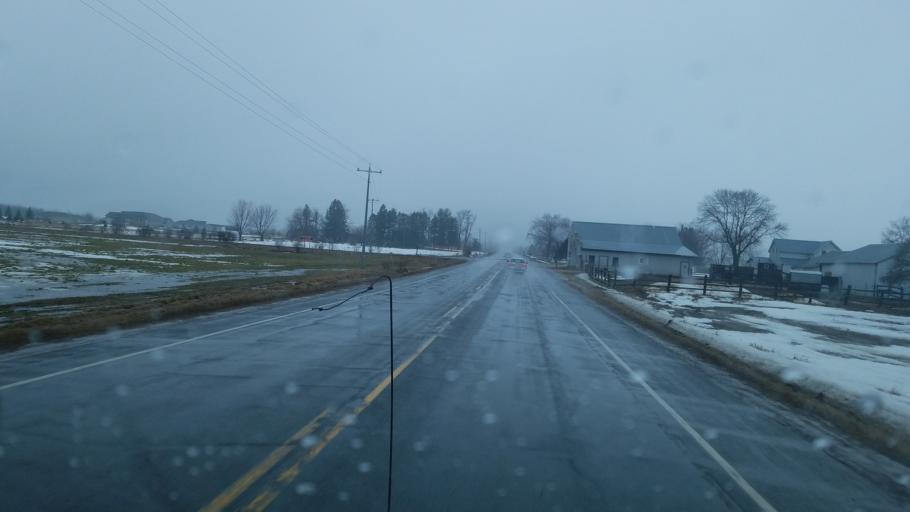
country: US
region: Wisconsin
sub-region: Wood County
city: Marshfield
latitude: 44.6777
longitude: -90.2368
